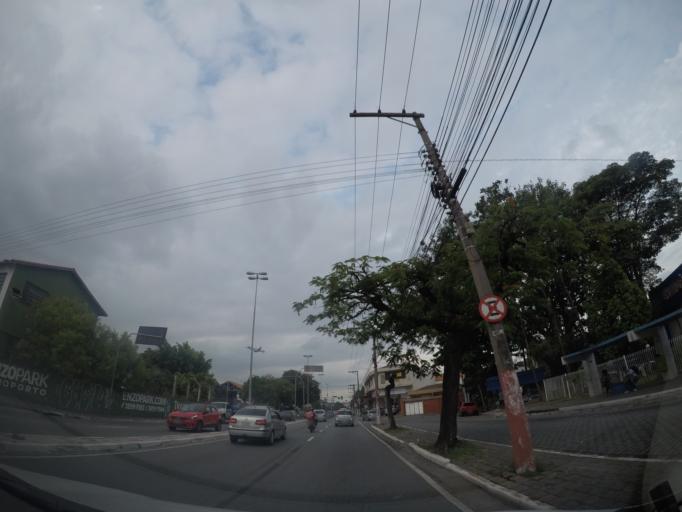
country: BR
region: Sao Paulo
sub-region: Guarulhos
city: Guarulhos
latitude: -23.4521
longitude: -46.5165
